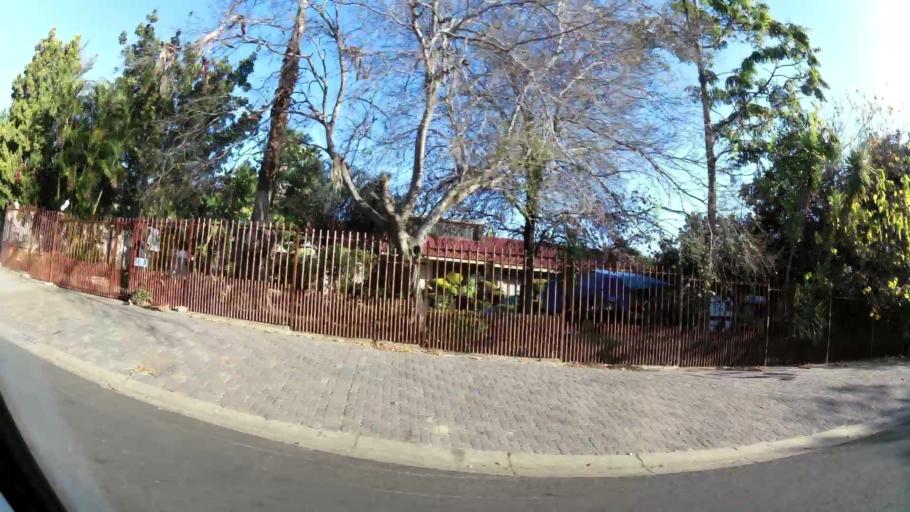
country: ZA
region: North-West
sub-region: Bojanala Platinum District Municipality
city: Rustenburg
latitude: -25.6865
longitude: 27.2361
